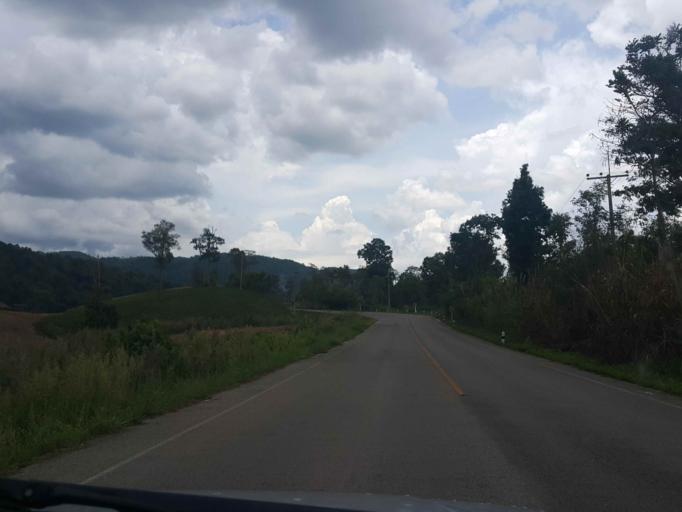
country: TH
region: Lampang
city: Ngao
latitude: 18.9354
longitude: 100.0843
